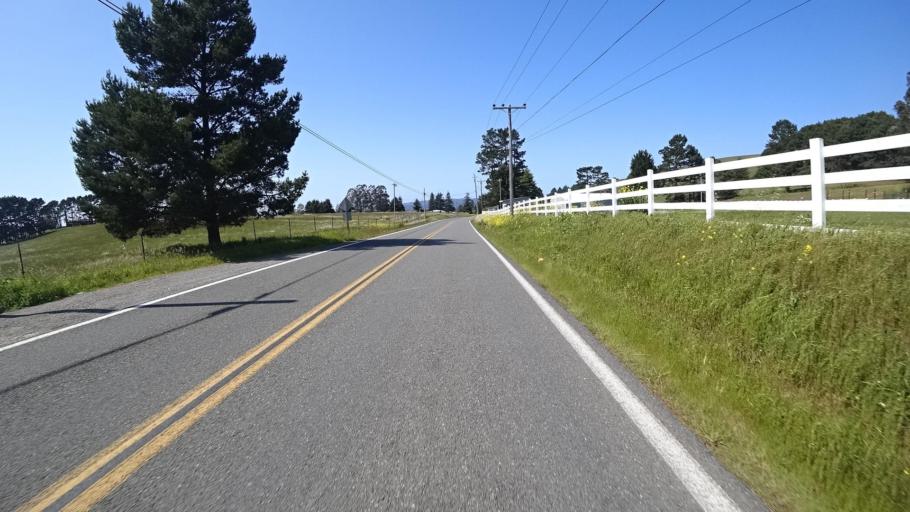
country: US
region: California
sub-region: Humboldt County
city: Hydesville
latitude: 40.5534
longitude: -124.1206
